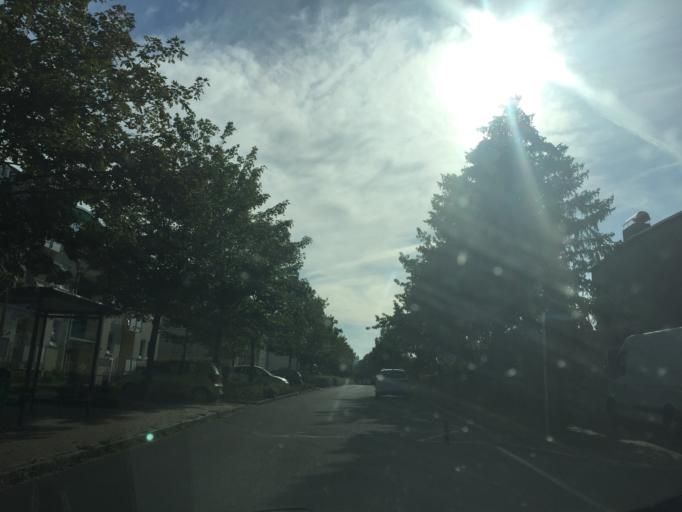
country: DE
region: Thuringia
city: Schmolln
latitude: 50.8882
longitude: 12.3635
